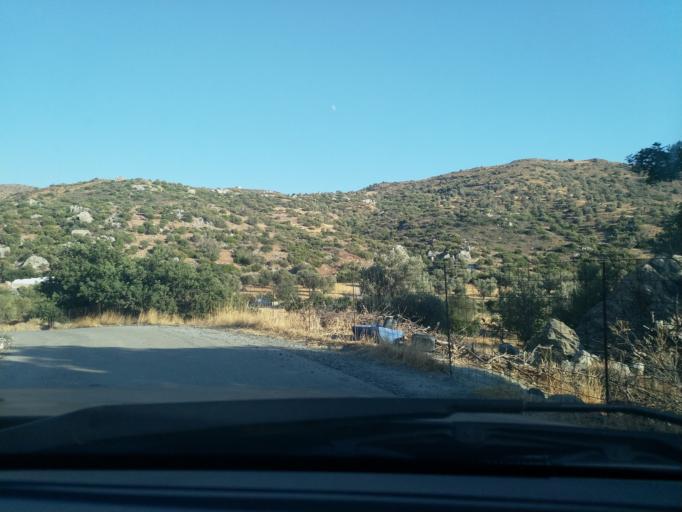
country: GR
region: Crete
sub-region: Nomos Rethymnis
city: Agia Galini
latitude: 35.1161
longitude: 24.5647
